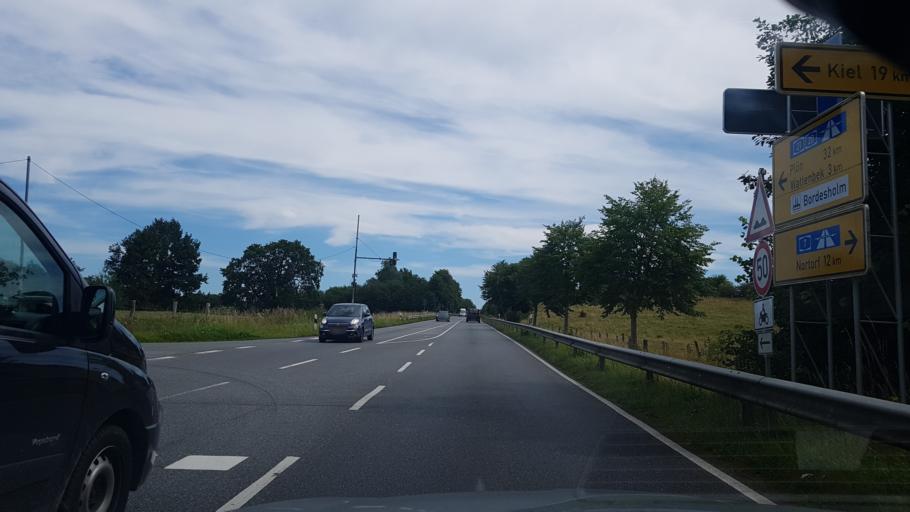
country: DE
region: Schleswig-Holstein
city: Bordesholm
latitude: 54.1876
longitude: 10.0261
